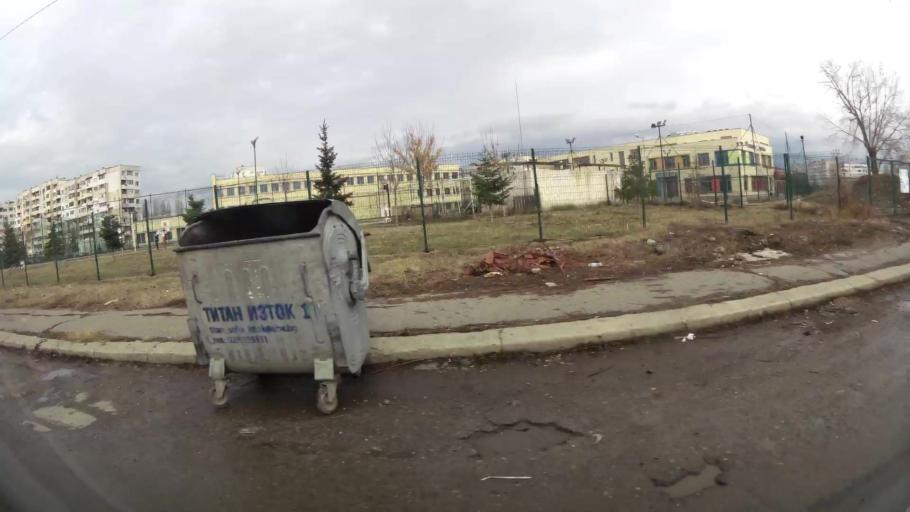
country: BG
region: Sofia-Capital
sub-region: Stolichna Obshtina
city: Sofia
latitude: 42.7448
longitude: 23.2733
